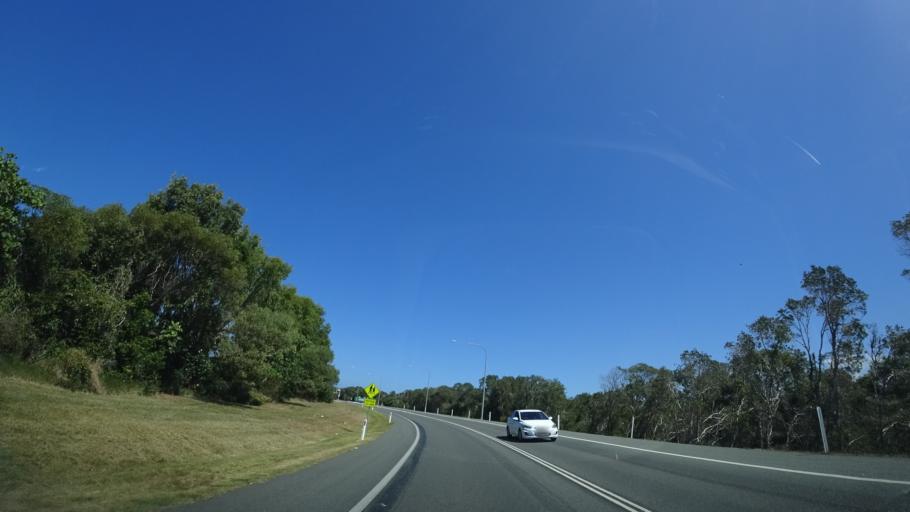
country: AU
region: Queensland
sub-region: Sunshine Coast
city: Coolum Beach
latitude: -26.5877
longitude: 153.0932
